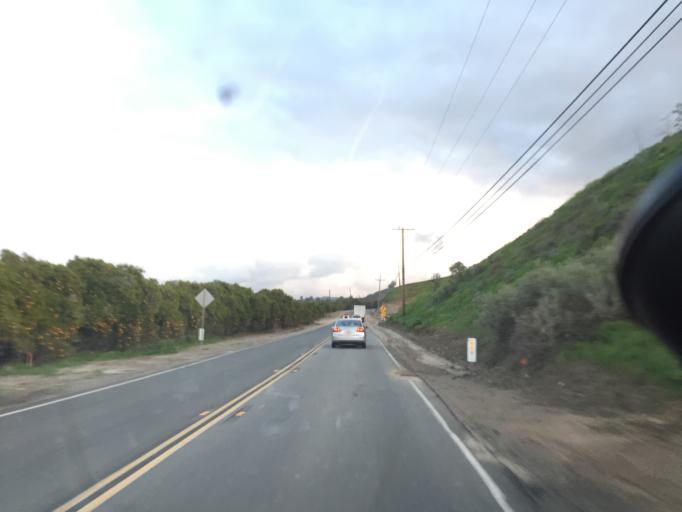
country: US
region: California
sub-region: San Bernardino County
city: Redlands
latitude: 34.0165
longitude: -117.1864
